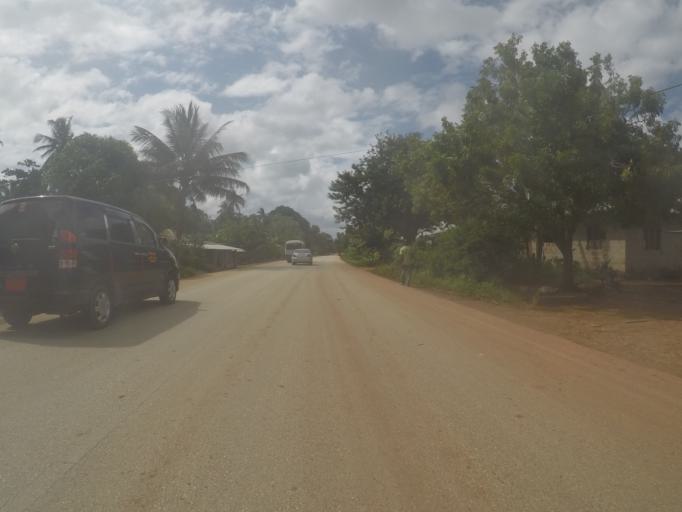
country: TZ
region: Zanzibar North
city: Mkokotoni
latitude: -5.8618
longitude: 39.2805
